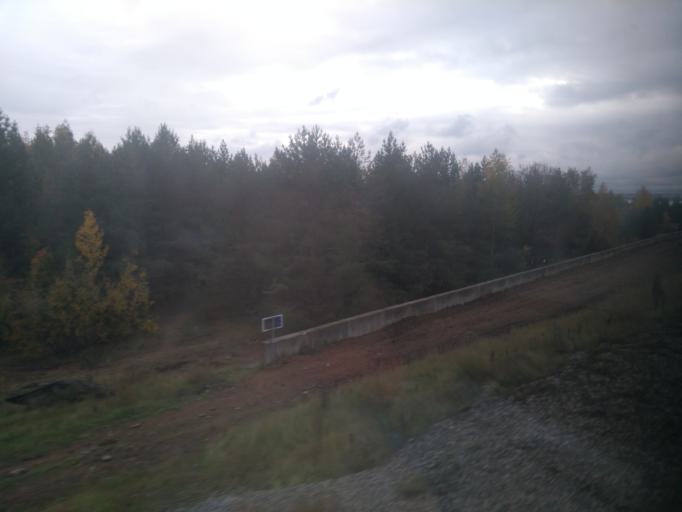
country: RU
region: Tatarstan
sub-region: Tukayevskiy Rayon
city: Naberezhnyye Chelny
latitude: 55.7232
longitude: 52.2595
